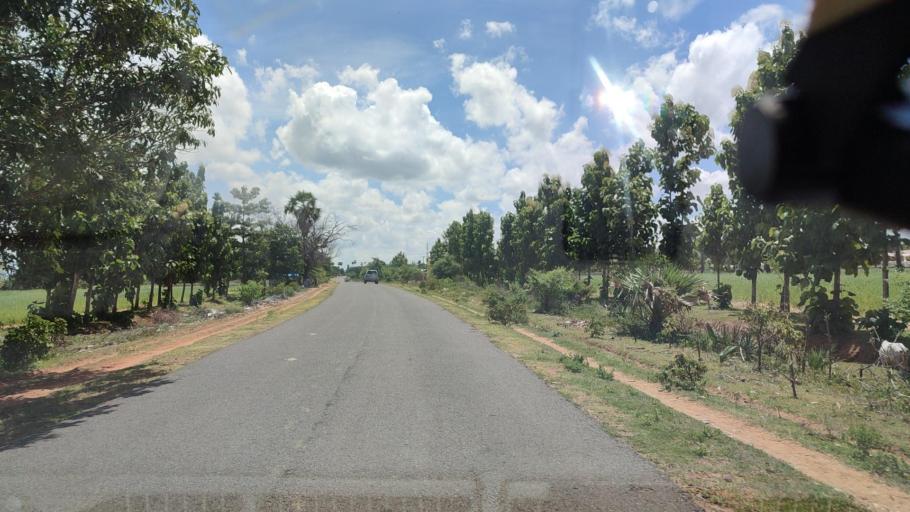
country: MM
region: Magway
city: Magway
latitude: 20.1904
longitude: 95.1756
